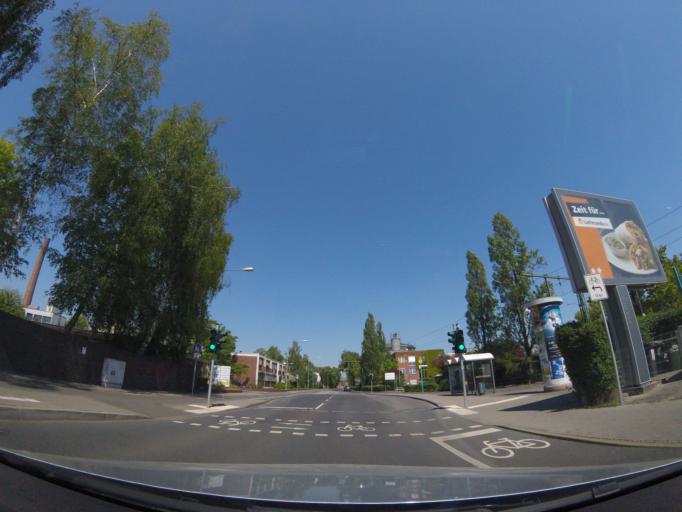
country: DE
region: Hesse
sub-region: Regierungsbezirk Darmstadt
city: Offenbach
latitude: 50.1283
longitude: 8.7675
